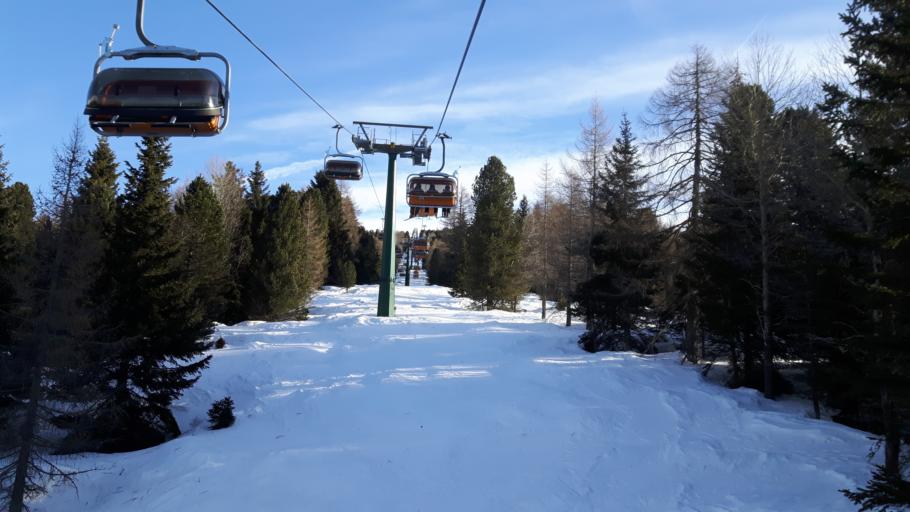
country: IT
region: Trentino-Alto Adige
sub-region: Provincia di Trento
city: Moena
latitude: 46.3330
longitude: 11.7029
